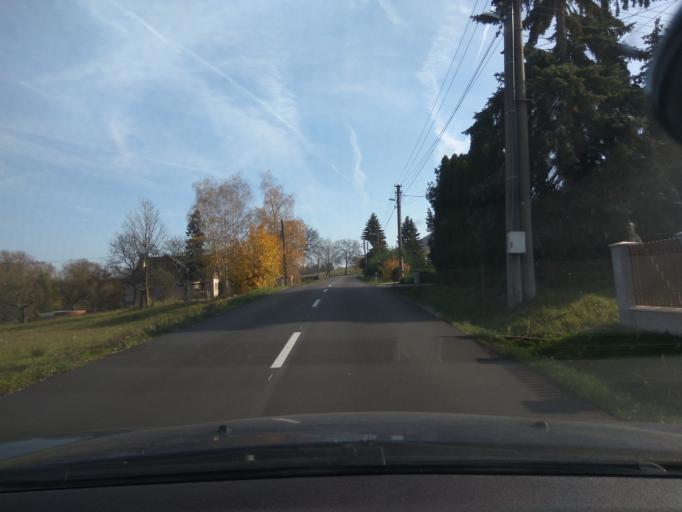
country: SK
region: Nitriansky
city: Brezova pod Bradlom
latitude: 48.6726
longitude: 17.5858
